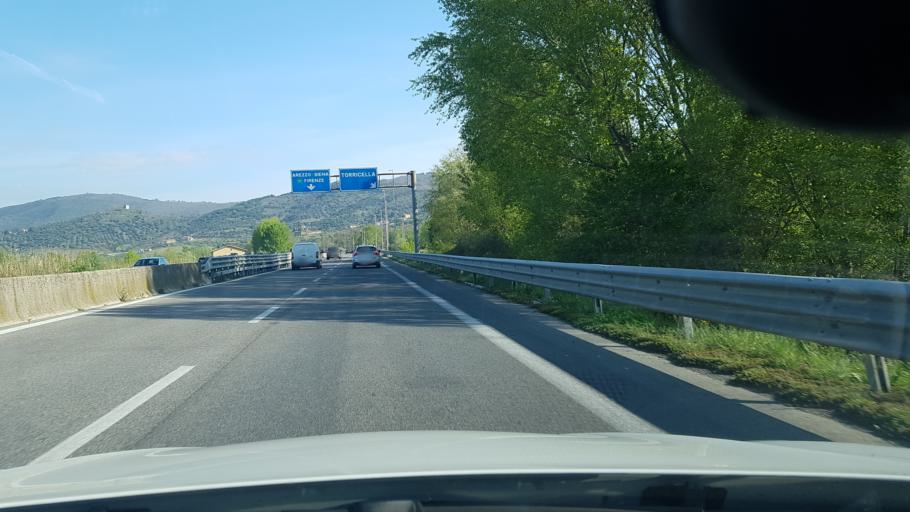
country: IT
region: Umbria
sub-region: Provincia di Perugia
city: Magione
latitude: 43.1659
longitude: 12.1893
